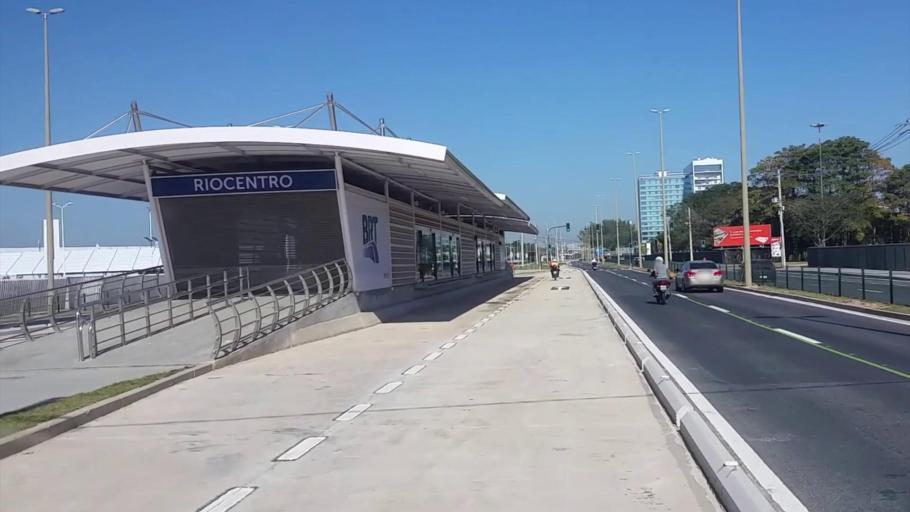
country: BR
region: Rio de Janeiro
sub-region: Nilopolis
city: Nilopolis
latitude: -22.9765
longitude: -43.4062
